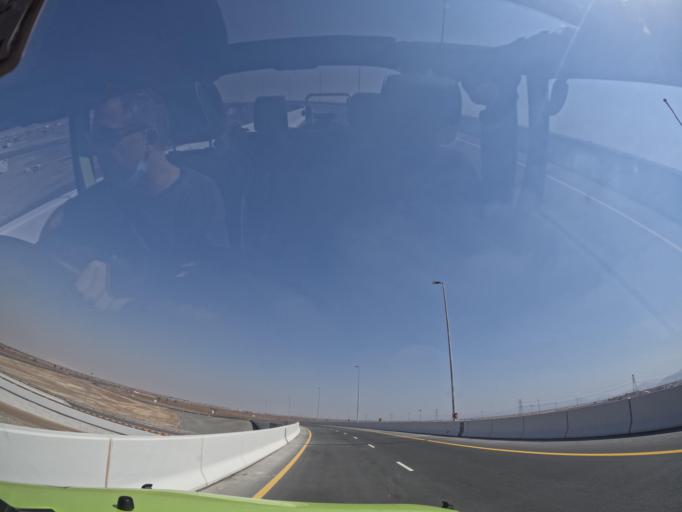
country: AE
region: Ash Shariqah
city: Adh Dhayd
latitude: 24.9089
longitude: 55.8026
